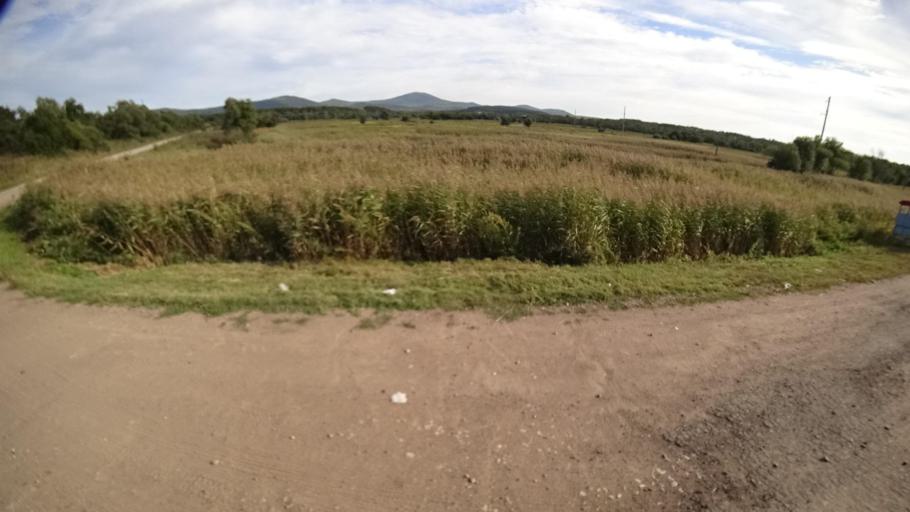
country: RU
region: Primorskiy
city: Dostoyevka
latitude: 44.3131
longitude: 133.4598
